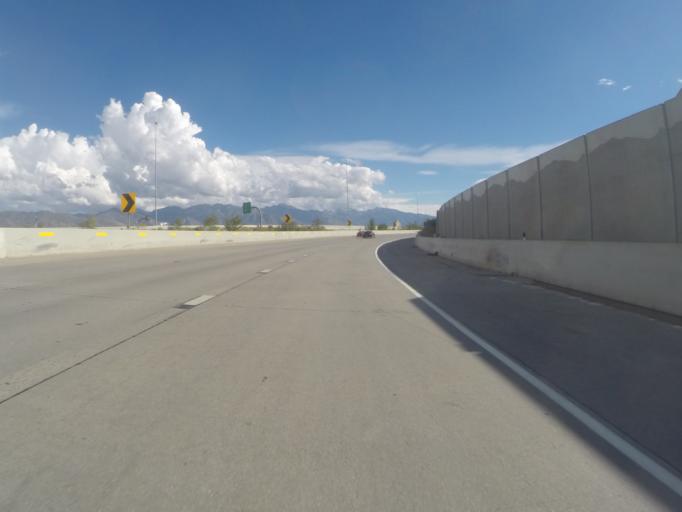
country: US
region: Utah
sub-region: Salt Lake County
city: Salt Lake City
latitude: 40.7634
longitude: -111.9160
